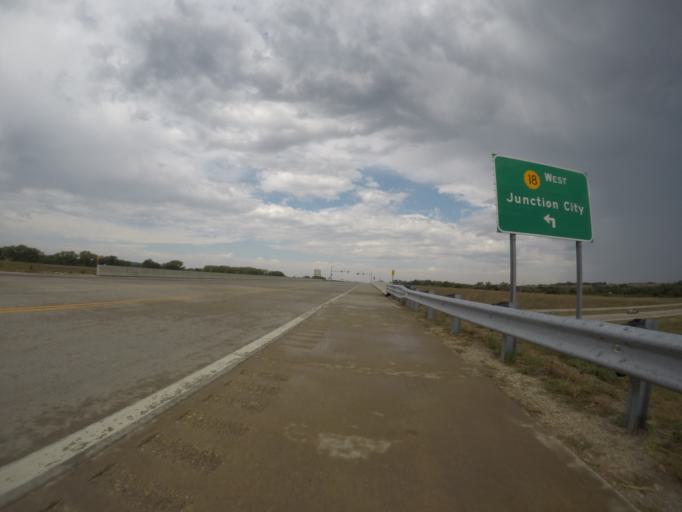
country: US
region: Kansas
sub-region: Riley County
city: Ogden
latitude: 39.1141
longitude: -96.6953
